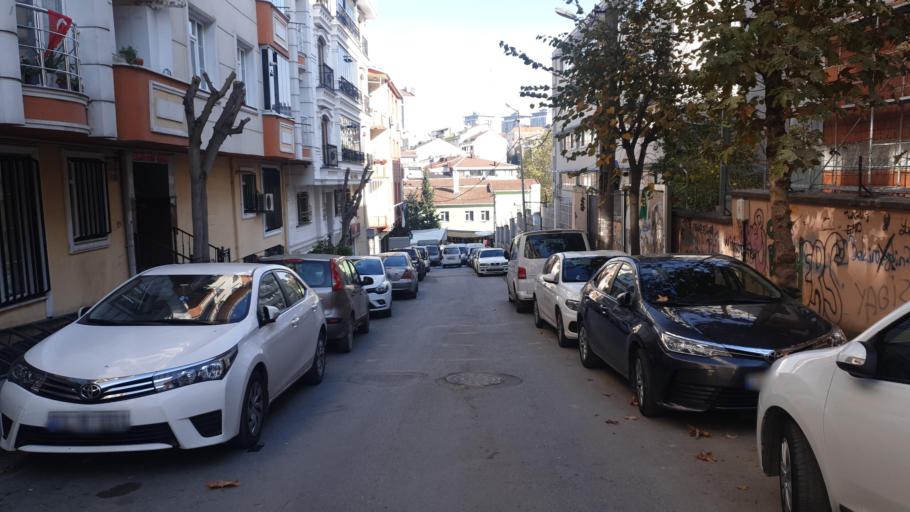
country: TR
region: Istanbul
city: Esenler
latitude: 41.0710
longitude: 28.9031
